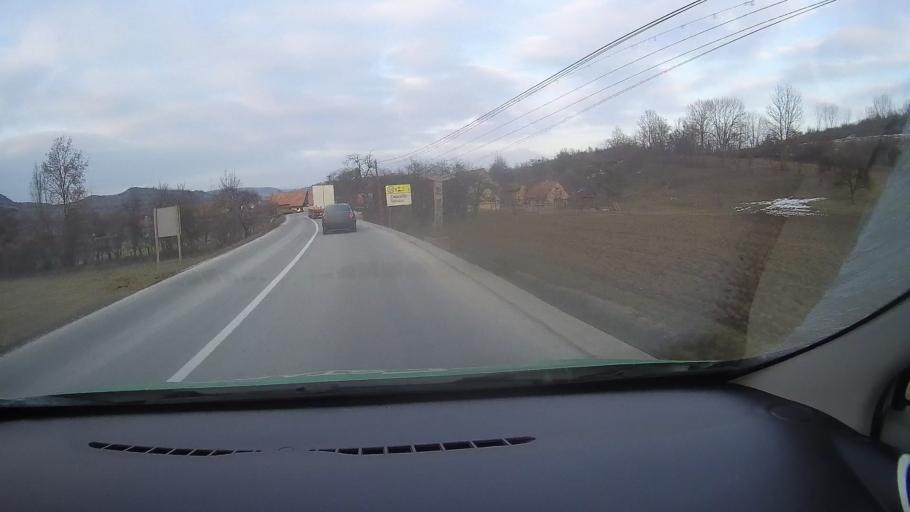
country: RO
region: Harghita
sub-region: Comuna Simonesti
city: Simonesti
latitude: 46.3448
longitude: 25.1186
